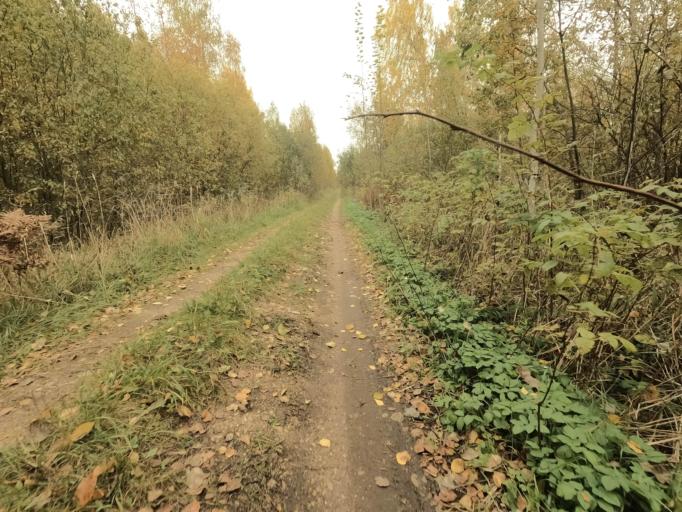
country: RU
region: Novgorod
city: Pankovka
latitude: 58.8906
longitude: 30.9497
